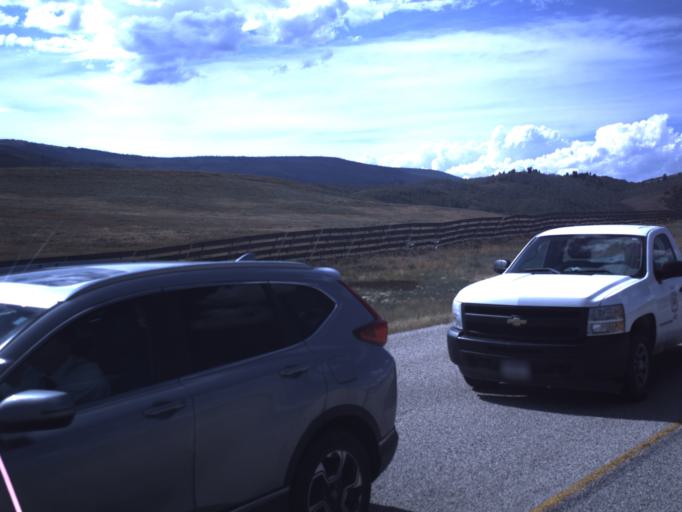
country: US
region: Utah
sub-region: Wasatch County
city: Heber
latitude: 40.2744
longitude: -111.2140
